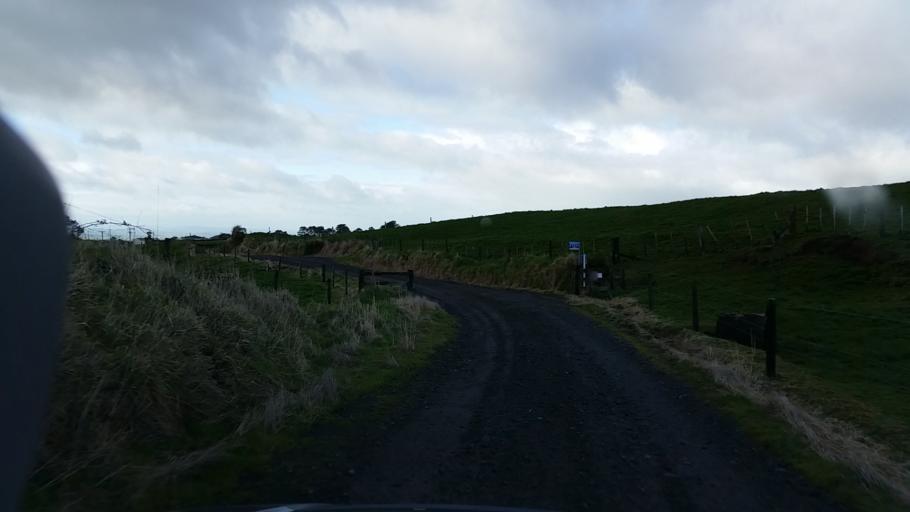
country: NZ
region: Taranaki
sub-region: South Taranaki District
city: Eltham
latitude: -39.3315
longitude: 174.1723
